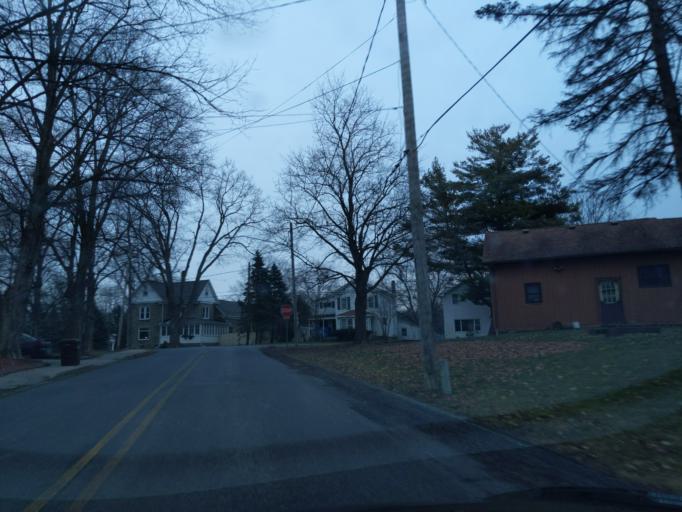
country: US
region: Michigan
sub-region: Ionia County
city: Portland
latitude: 42.9835
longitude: -84.9450
